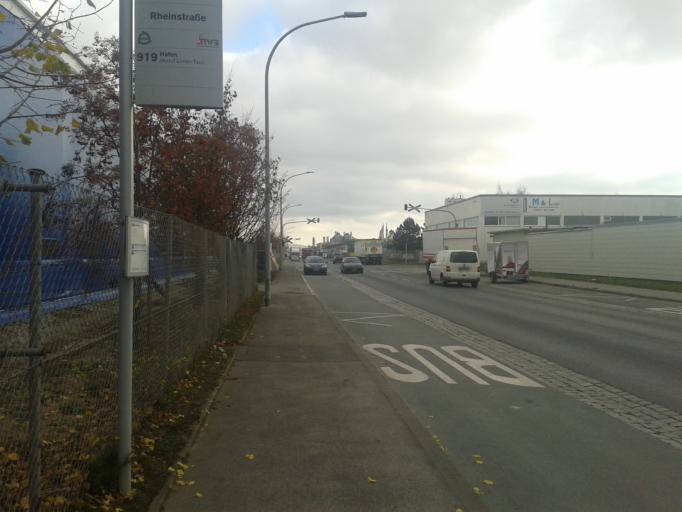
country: DE
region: Bavaria
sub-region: Upper Franconia
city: Hallstadt
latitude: 49.9122
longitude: 10.8653
